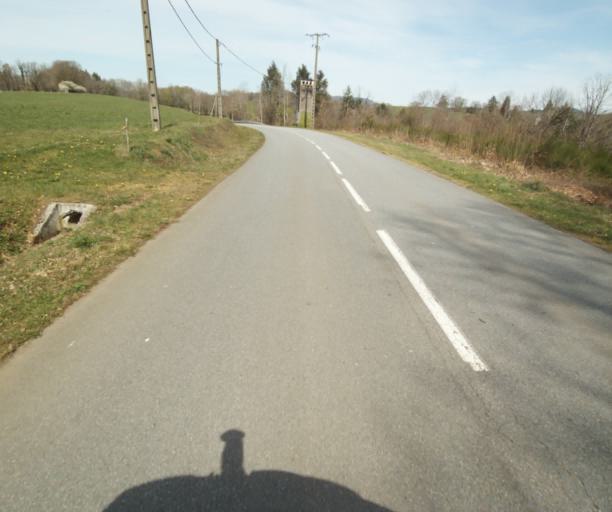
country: FR
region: Limousin
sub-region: Departement de la Correze
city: Correze
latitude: 45.3791
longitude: 1.8031
